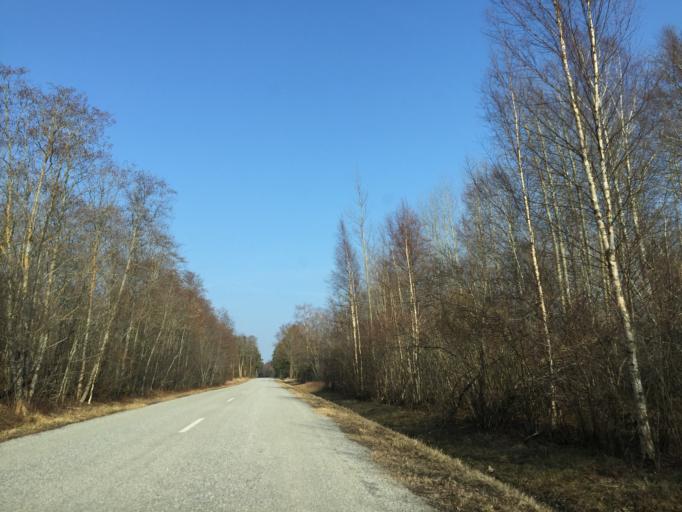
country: EE
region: Saare
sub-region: Orissaare vald
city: Orissaare
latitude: 58.5585
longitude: 23.3272
